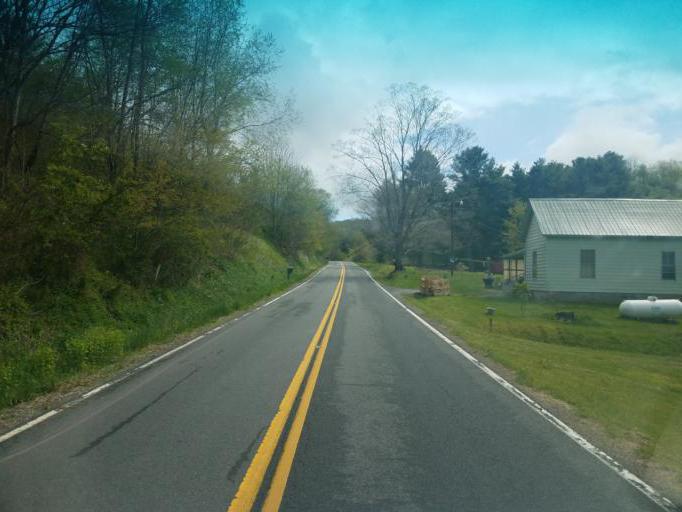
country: US
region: Virginia
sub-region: Smyth County
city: Atkins
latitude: 36.9854
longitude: -81.3940
